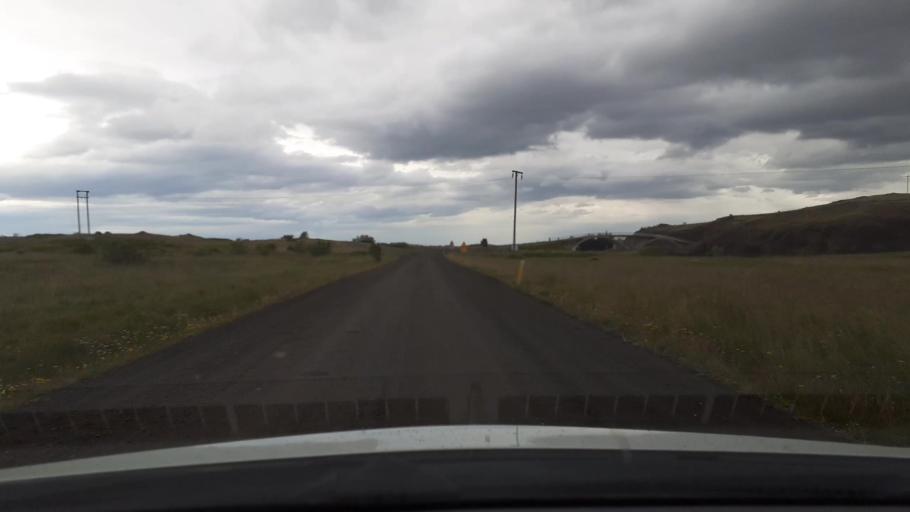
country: IS
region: West
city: Borgarnes
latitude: 64.6034
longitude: -21.7029
